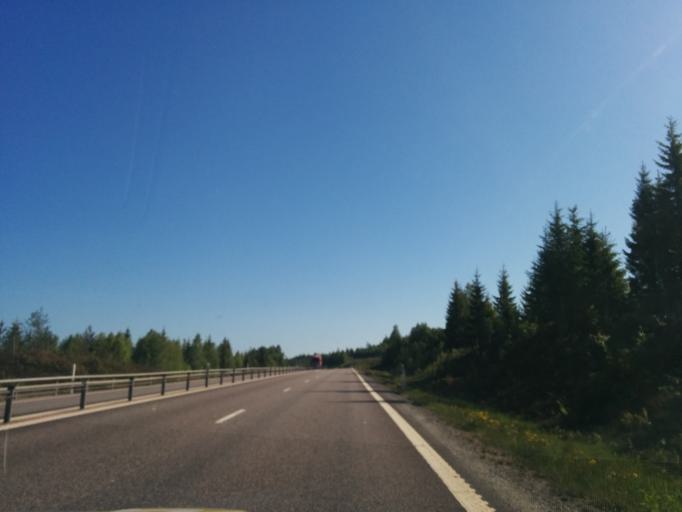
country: SE
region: Vaesternorrland
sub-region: Haernoesands Kommun
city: Haernoesand
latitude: 62.7192
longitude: 17.9156
